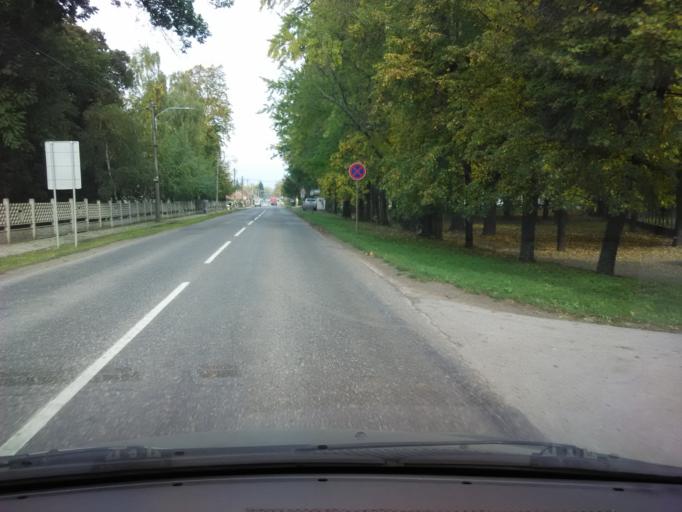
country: SK
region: Nitriansky
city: Levice
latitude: 48.1966
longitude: 18.5174
